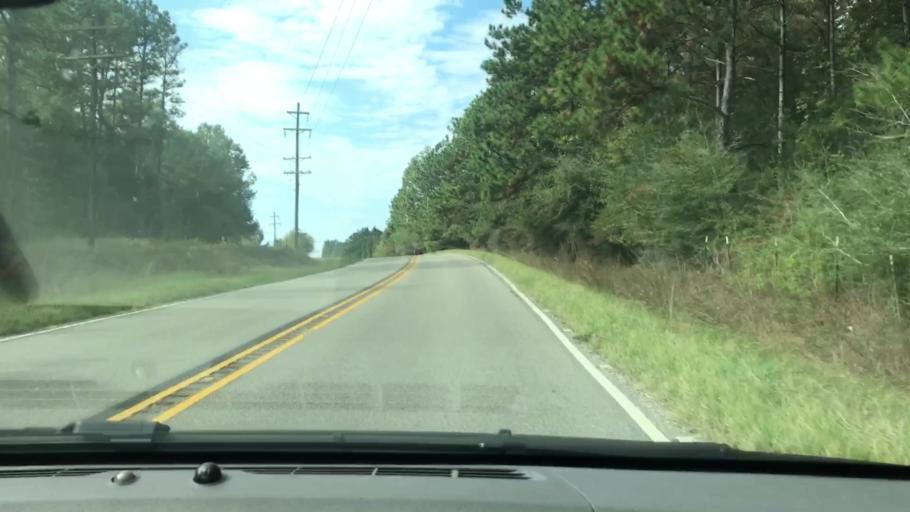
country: US
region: Louisiana
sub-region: Saint Tammany Parish
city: Abita Springs
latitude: 30.5338
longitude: -89.9044
